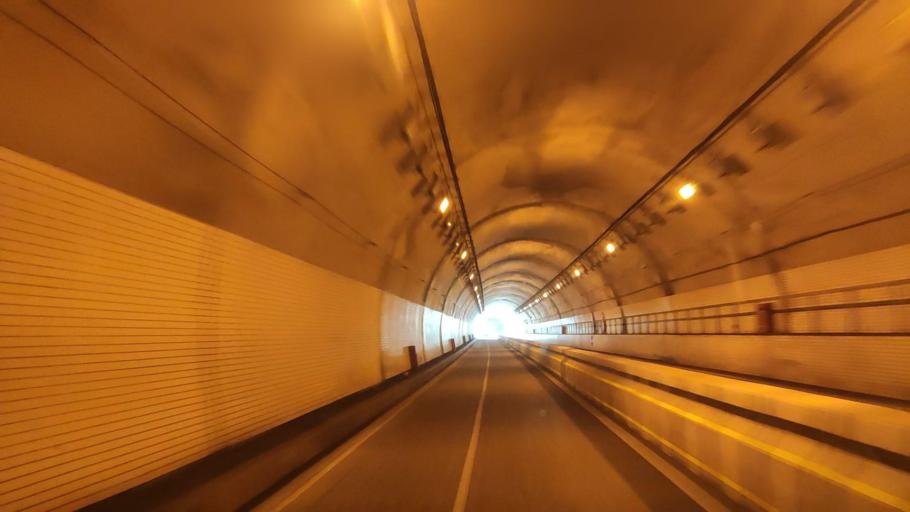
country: JP
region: Toyama
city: Nyuzen
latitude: 36.9549
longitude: 137.5765
